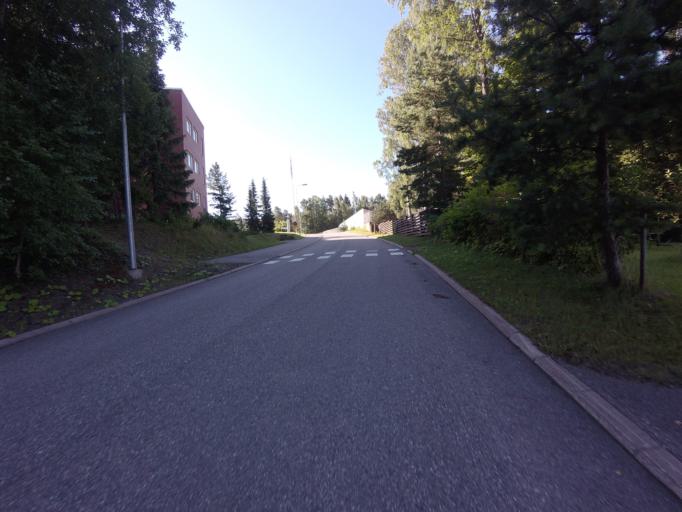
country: FI
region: Uusimaa
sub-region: Helsinki
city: Kauniainen
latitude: 60.1593
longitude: 24.7027
